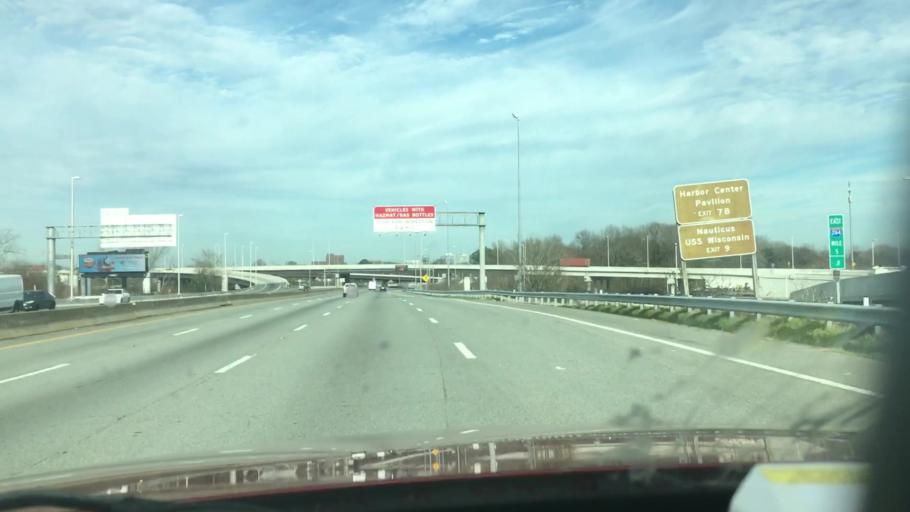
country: US
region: Virginia
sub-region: City of Portsmouth
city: Portsmouth
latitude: 36.8243
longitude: -76.3288
